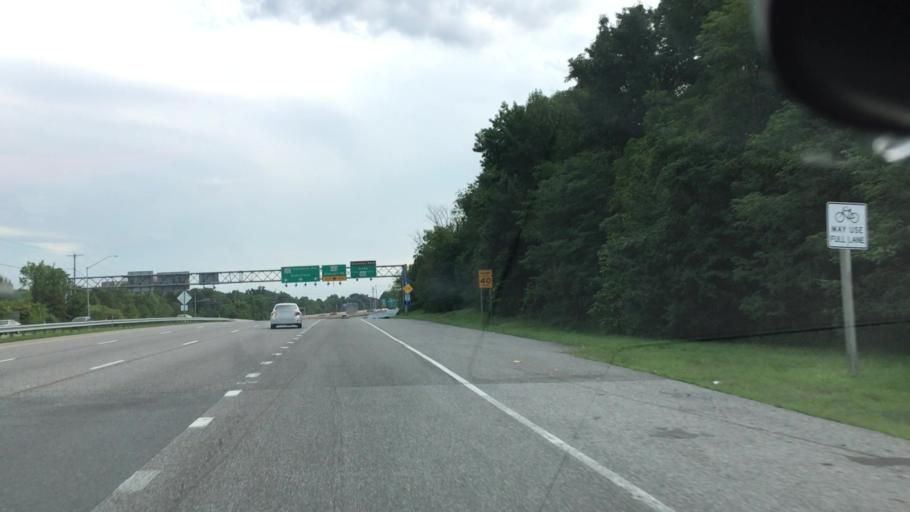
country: US
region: Maryland
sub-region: Prince George's County
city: Berwyn Heights
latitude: 39.0006
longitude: -76.8973
